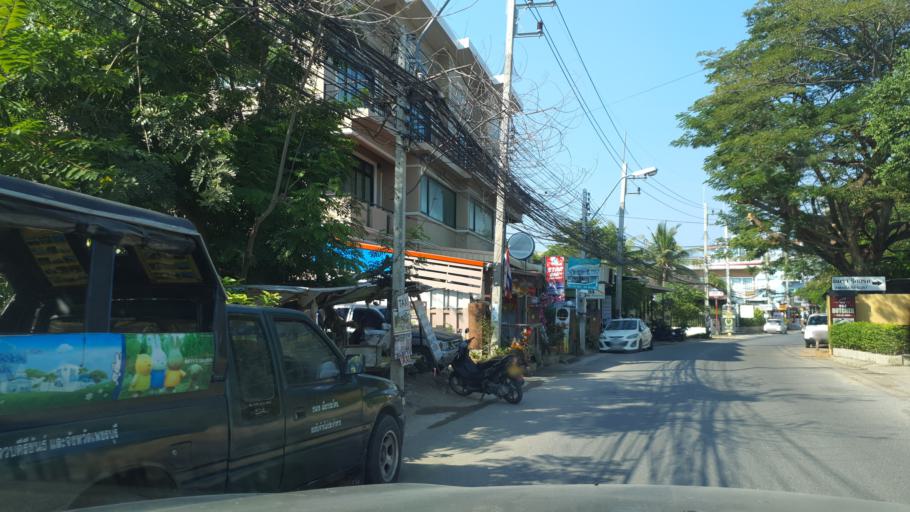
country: TH
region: Prachuap Khiri Khan
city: Hua Hin
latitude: 12.5544
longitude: 99.9556
